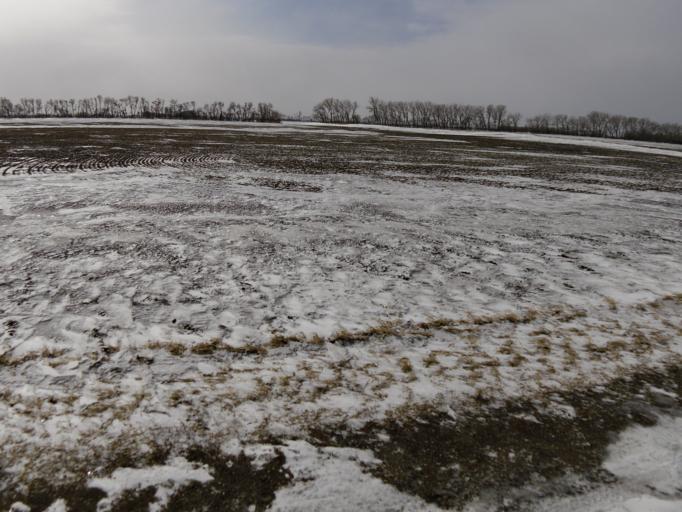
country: US
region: North Dakota
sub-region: Walsh County
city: Grafton
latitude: 48.3976
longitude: -97.1998
